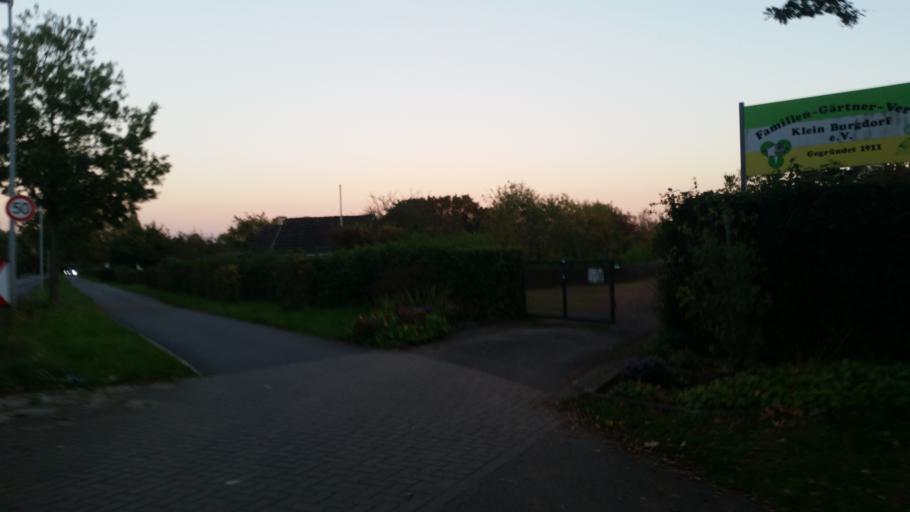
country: DE
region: Lower Saxony
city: Hannover
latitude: 52.3995
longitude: 9.7038
